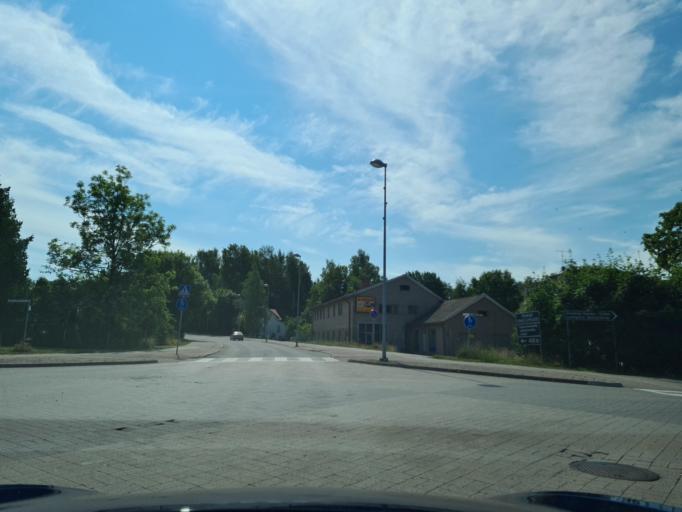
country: FI
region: Varsinais-Suomi
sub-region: Turku
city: Paimio
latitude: 60.4508
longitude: 22.6938
